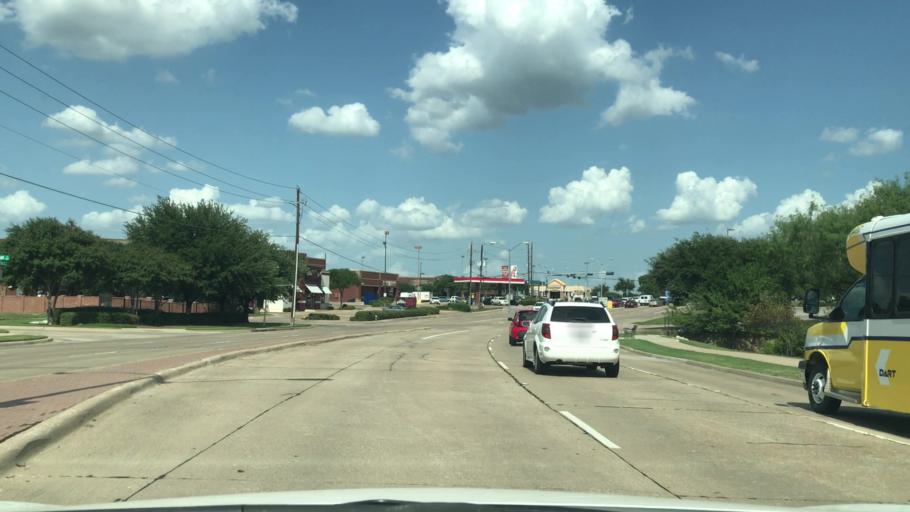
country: US
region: Texas
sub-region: Dallas County
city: Carrollton
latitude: 32.9733
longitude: -96.8921
